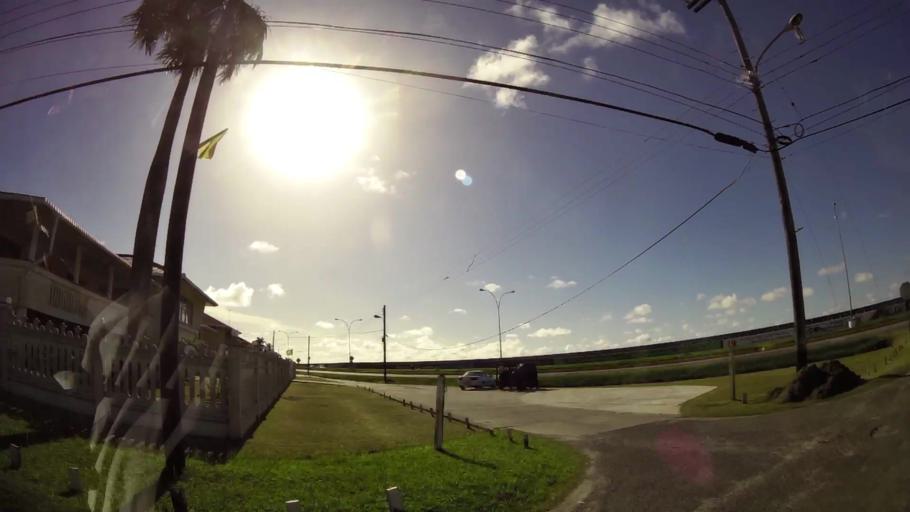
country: GY
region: Demerara-Mahaica
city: Georgetown
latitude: 6.8248
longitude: -58.1352
